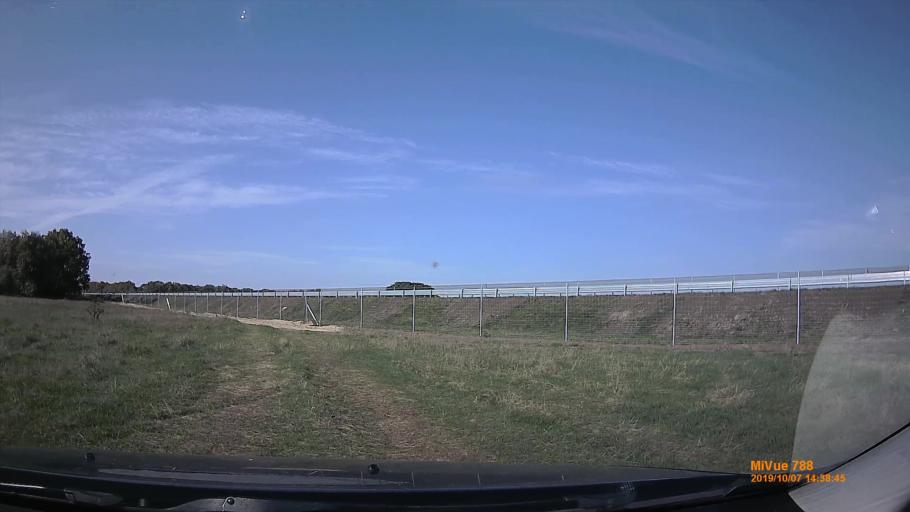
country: HU
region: Jasz-Nagykun-Szolnok
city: Kunszentmarton
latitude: 46.8544
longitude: 20.3130
